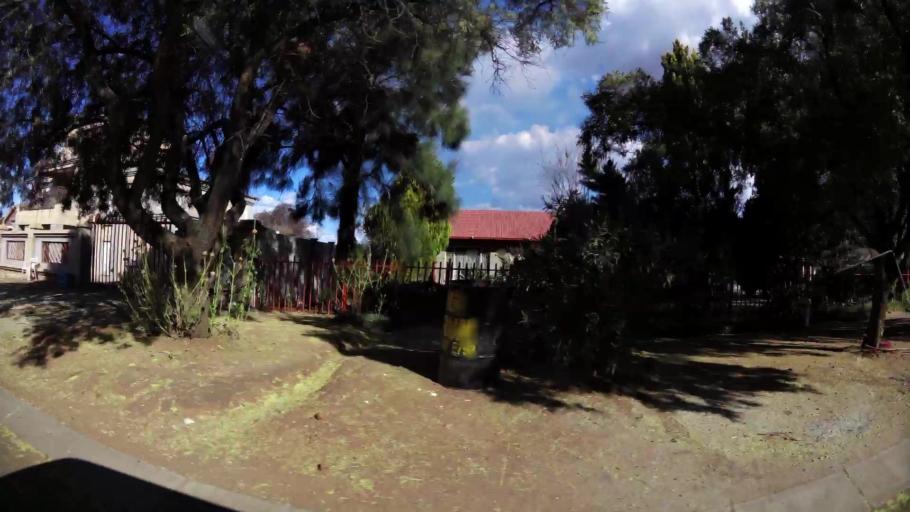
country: ZA
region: North-West
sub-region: Dr Kenneth Kaunda District Municipality
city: Klerksdorp
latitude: -26.8213
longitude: 26.6580
